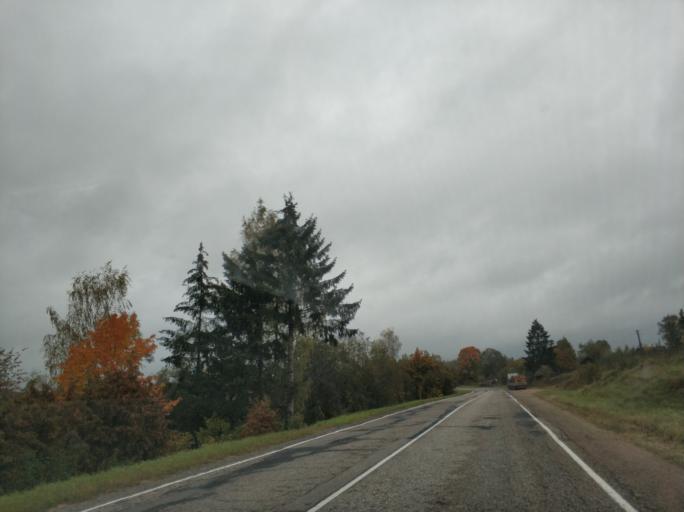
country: RU
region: Pskov
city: Sebezh
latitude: 56.2894
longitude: 28.5844
